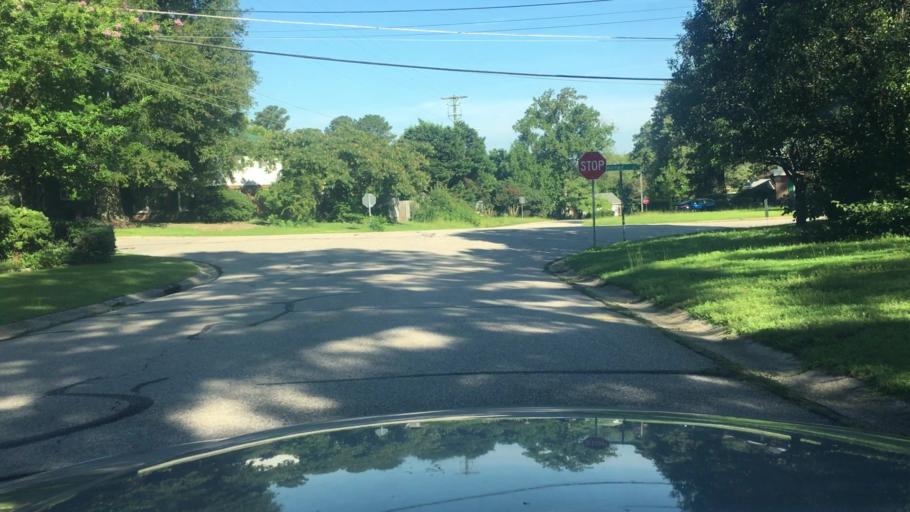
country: US
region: North Carolina
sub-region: Cumberland County
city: Fayetteville
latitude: 35.1365
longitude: -78.8921
